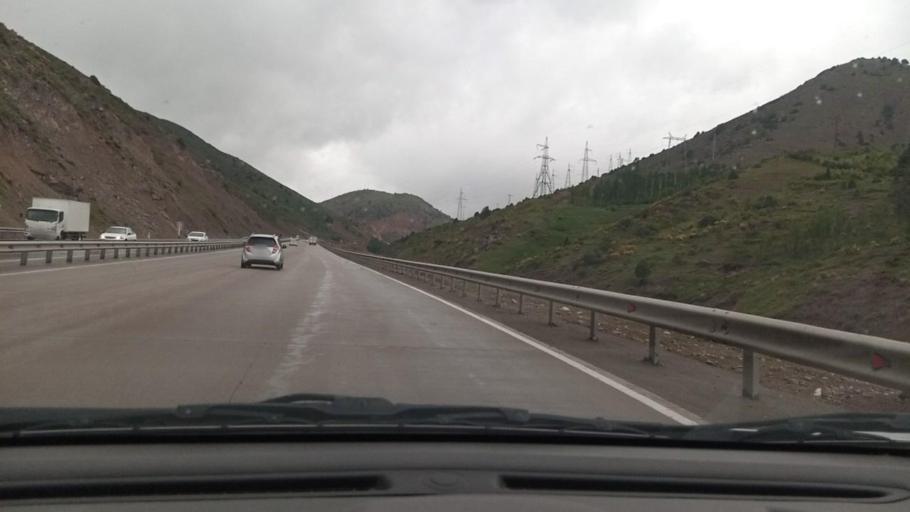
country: UZ
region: Toshkent
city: Angren
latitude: 41.0539
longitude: 70.5660
